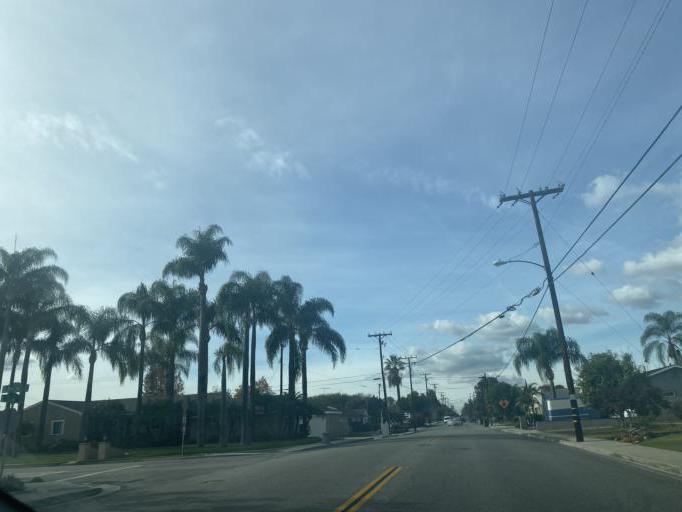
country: US
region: California
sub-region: Orange County
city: Brea
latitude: 33.9089
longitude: -117.8907
